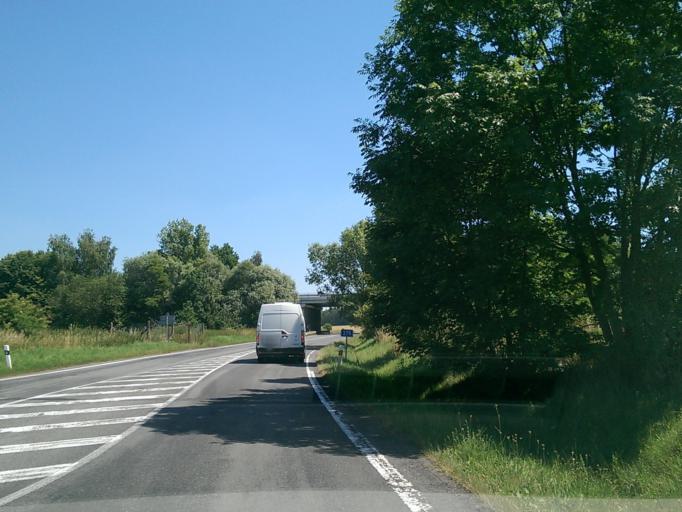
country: CZ
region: Central Bohemia
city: Benatky nad Jizerou
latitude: 50.3224
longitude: 14.8696
